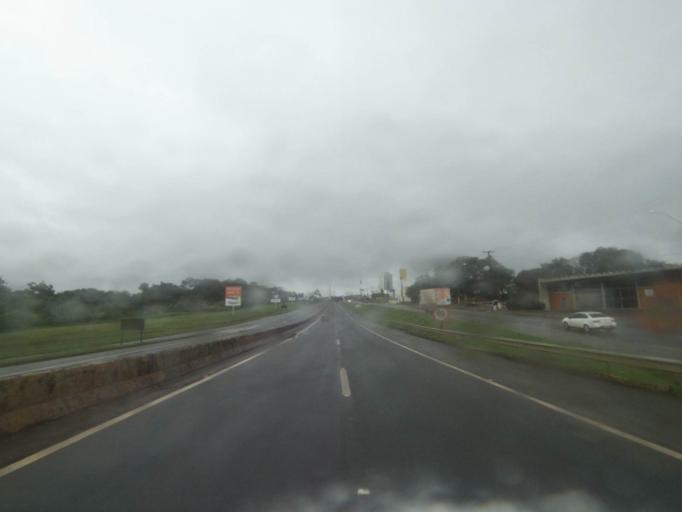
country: PY
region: Alto Parana
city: Ciudad del Este
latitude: -25.5078
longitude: -54.5831
